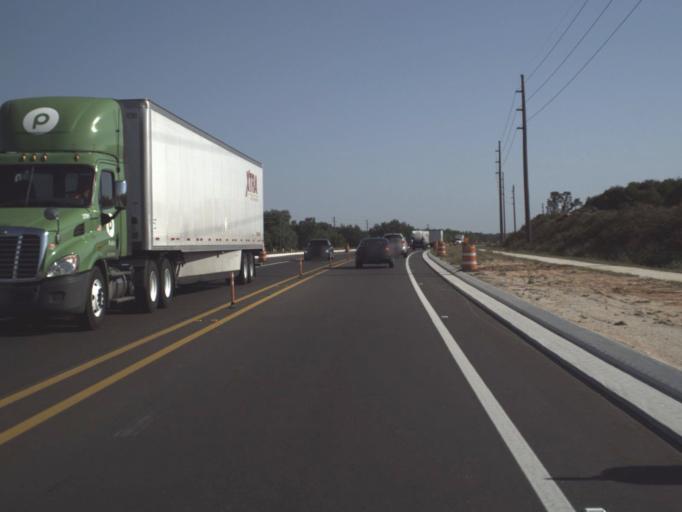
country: US
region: Florida
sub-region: Lake County
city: Clermont
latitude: 28.4656
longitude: -81.7196
